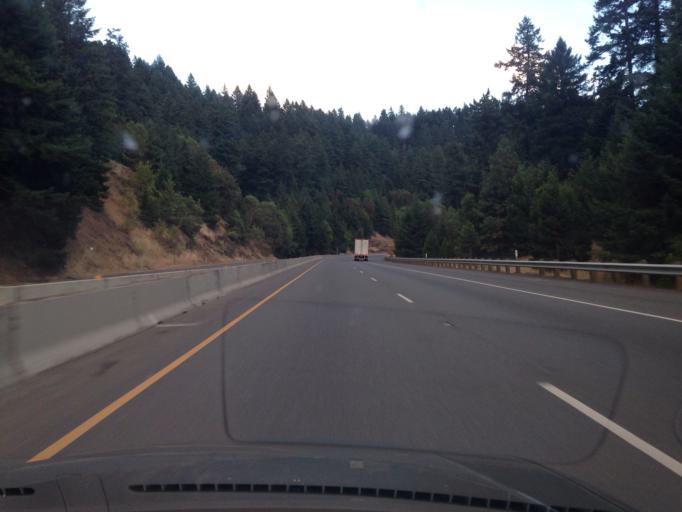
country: US
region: Oregon
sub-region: Douglas County
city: Canyonville
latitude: 42.7394
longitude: -123.3712
